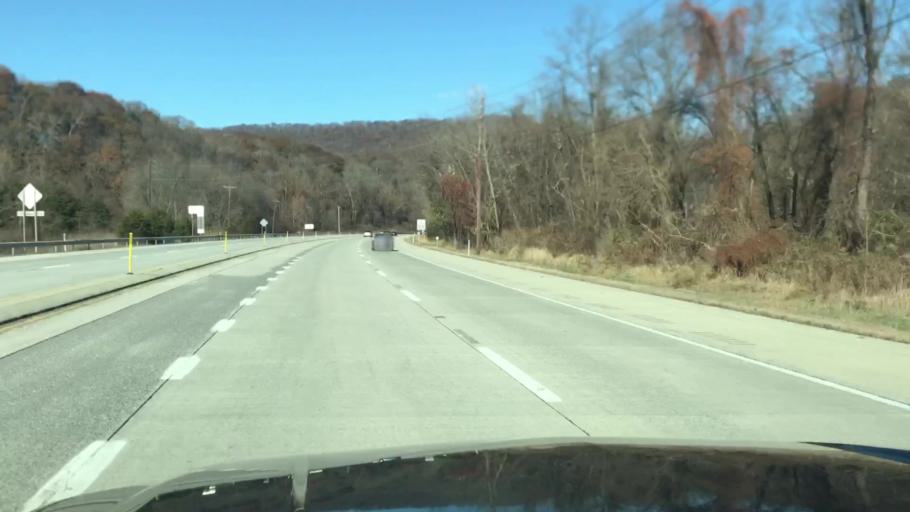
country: US
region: Pennsylvania
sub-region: Dauphin County
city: Millersburg
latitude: 40.5063
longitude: -76.9803
